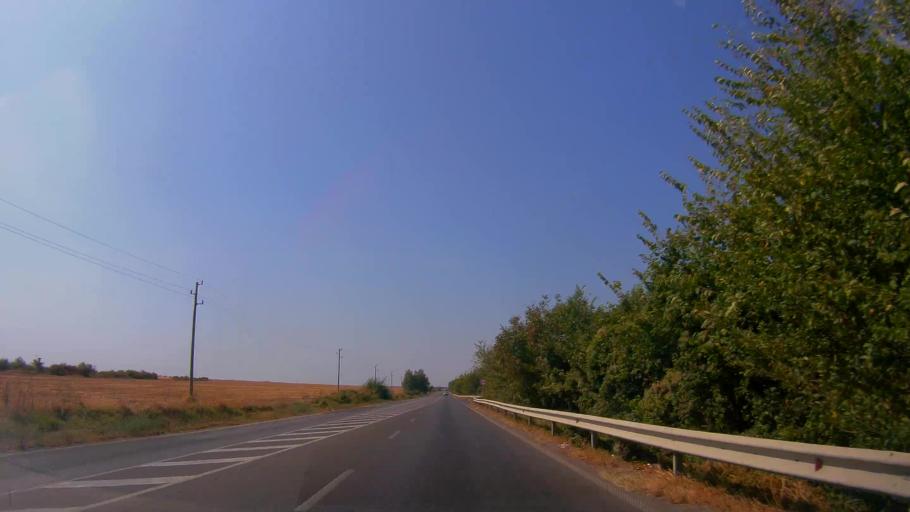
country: BG
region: Ruse
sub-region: Obshtina Vetovo
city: Senovo
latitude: 43.5619
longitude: 26.3542
